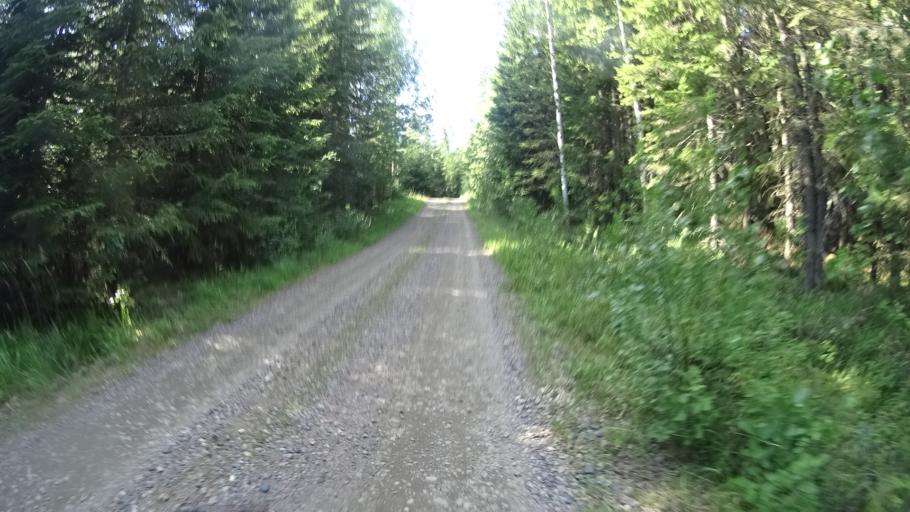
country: FI
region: Uusimaa
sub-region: Helsinki
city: Karkkila
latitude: 60.6456
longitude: 24.1661
